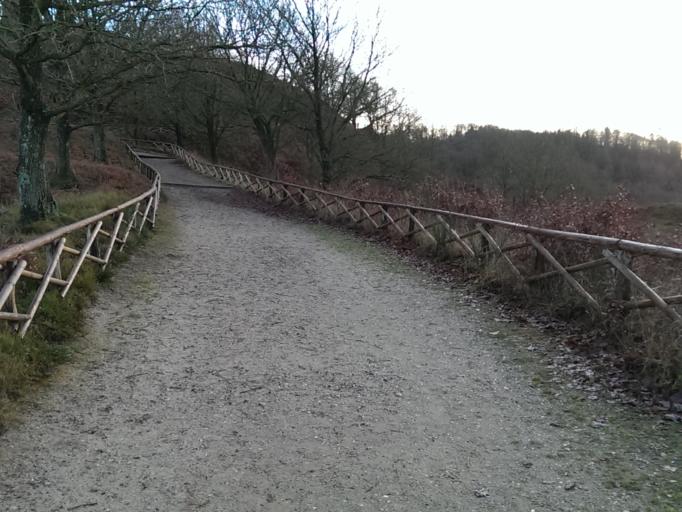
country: DK
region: Central Jutland
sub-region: Silkeborg Kommune
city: Svejbaek
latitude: 56.1072
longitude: 9.6832
